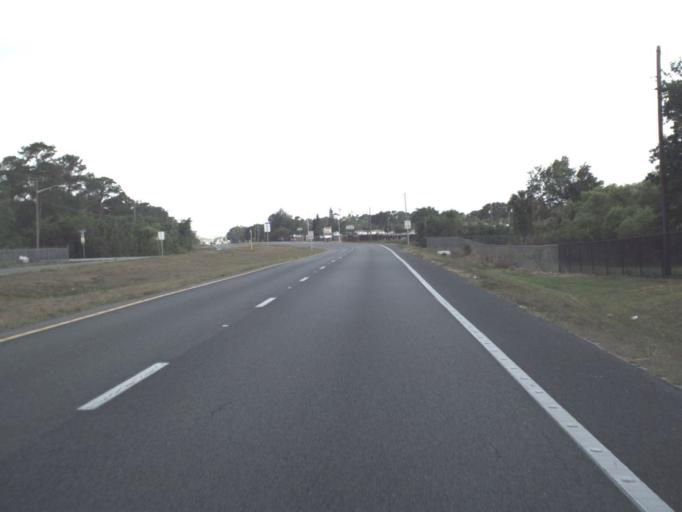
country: US
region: Florida
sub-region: Brevard County
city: Mims
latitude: 28.6937
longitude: -80.8581
